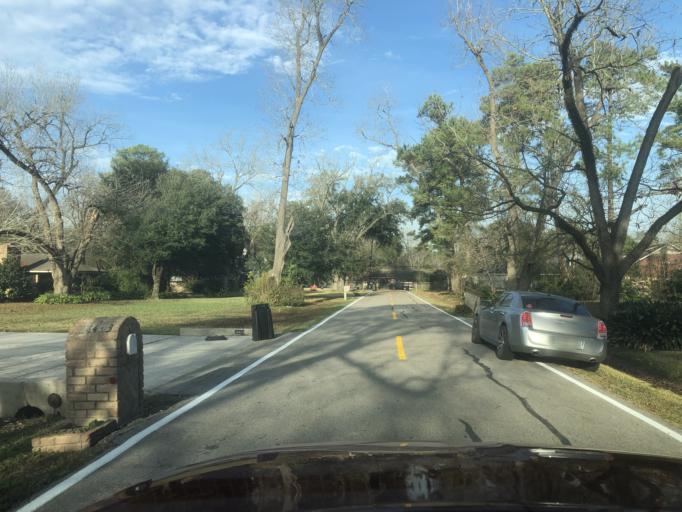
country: US
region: Texas
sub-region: Harris County
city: Spring
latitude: 30.0131
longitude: -95.4710
